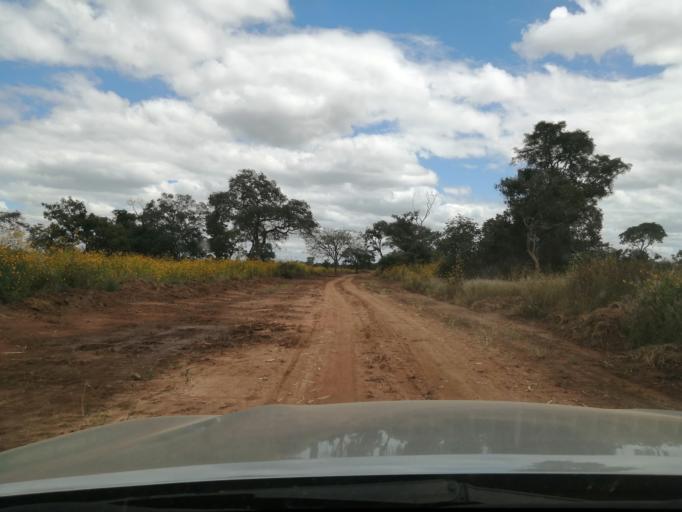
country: ZM
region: Central
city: Mumbwa
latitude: -14.5811
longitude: 27.2224
